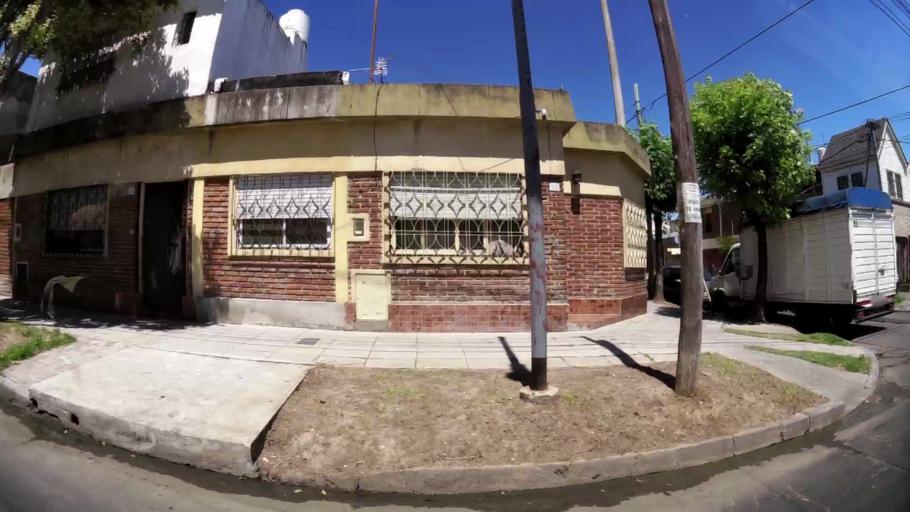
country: AR
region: Buenos Aires
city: Caseros
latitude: -34.5833
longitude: -58.5677
